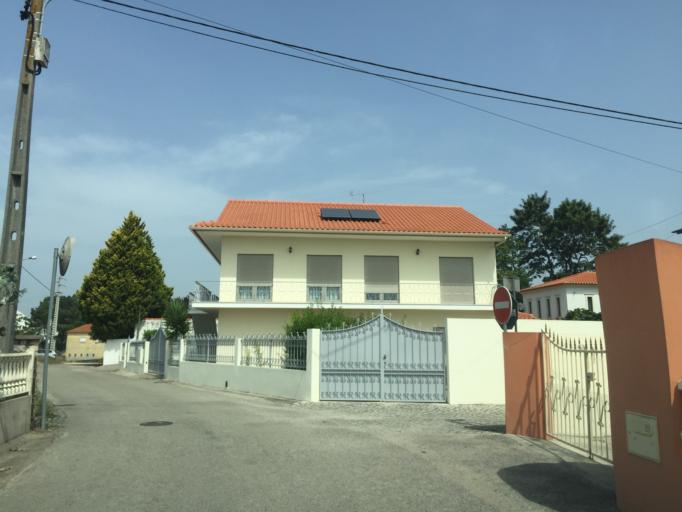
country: PT
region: Leiria
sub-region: Leiria
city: Monte Redondo
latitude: 39.9459
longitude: -8.7884
